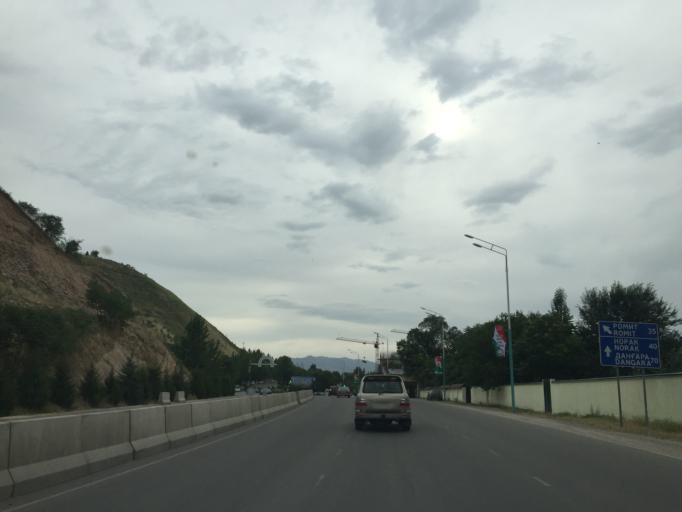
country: TJ
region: Republican Subordination
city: Vahdat
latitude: 38.5578
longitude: 68.9977
